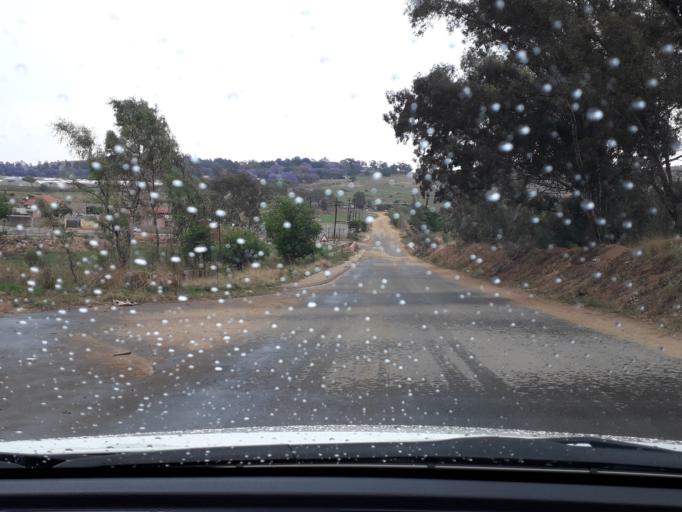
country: ZA
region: Gauteng
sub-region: West Rand District Municipality
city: Muldersdriseloop
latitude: -26.0037
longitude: 27.8547
